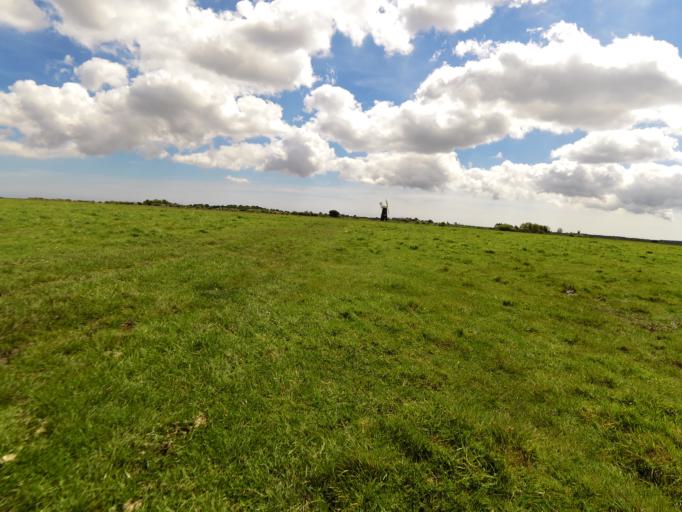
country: GB
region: England
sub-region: Norfolk
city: Acle
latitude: 52.5888
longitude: 1.6326
